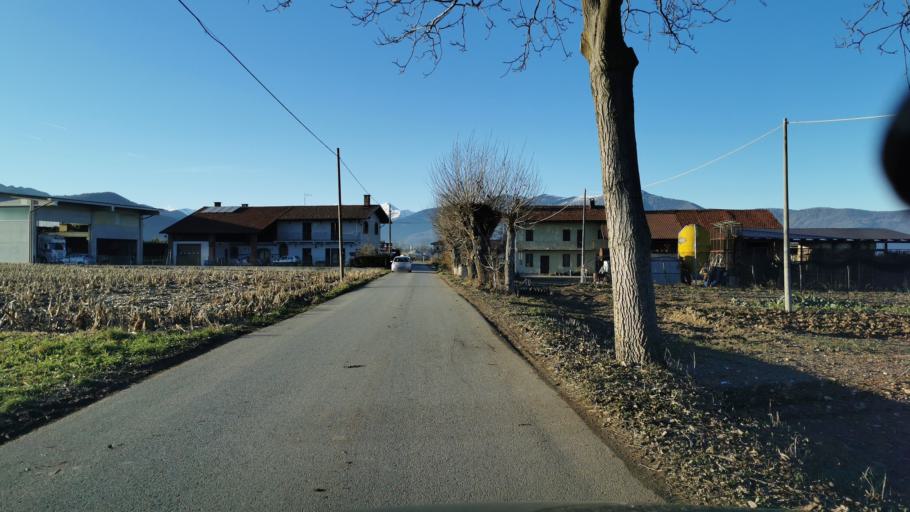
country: IT
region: Piedmont
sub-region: Provincia di Cuneo
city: Caraglio
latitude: 44.4317
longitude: 7.4434
